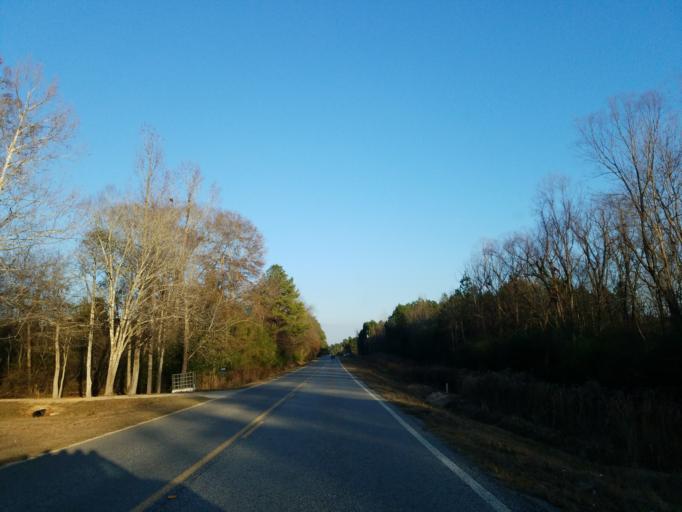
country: US
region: Mississippi
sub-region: Clarke County
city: Stonewall
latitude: 32.1668
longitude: -88.8551
